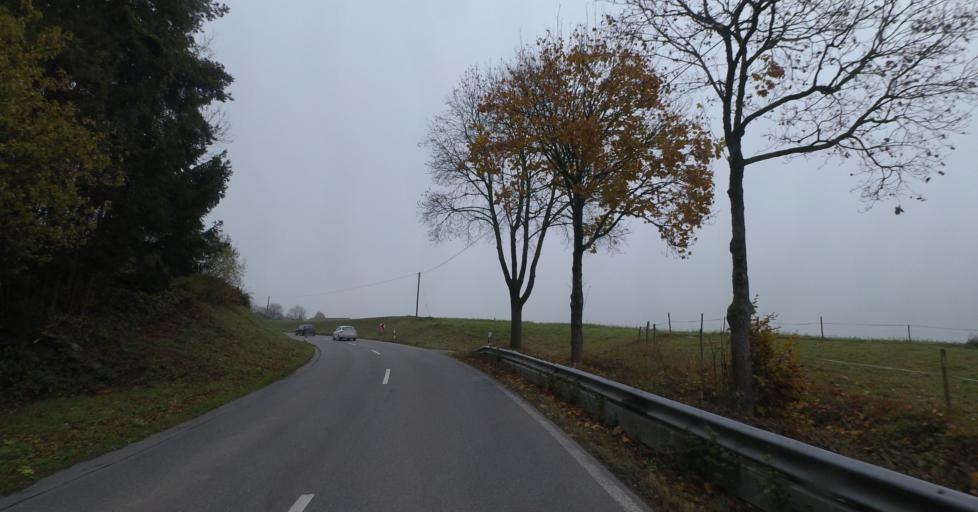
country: DE
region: Bavaria
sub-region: Upper Bavaria
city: Seeon-Seebruck
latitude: 47.9642
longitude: 12.5208
